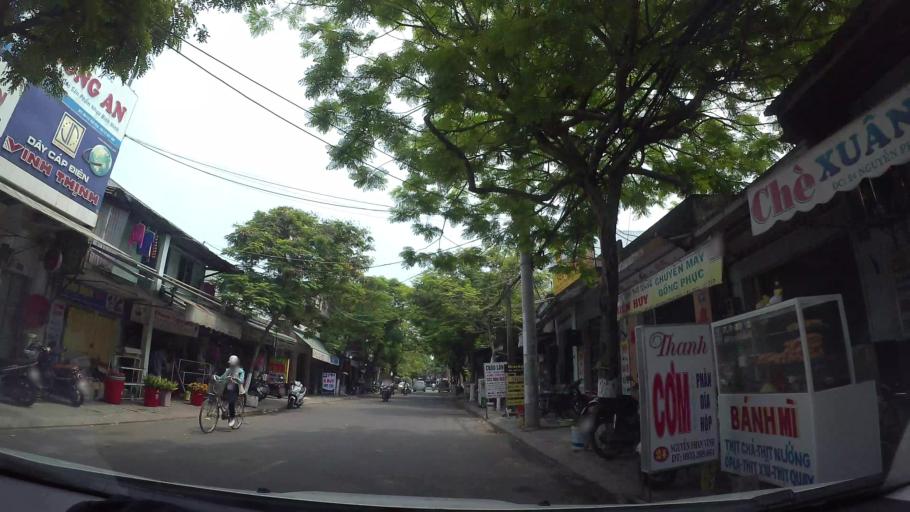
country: VN
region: Da Nang
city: Son Tra
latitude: 16.1009
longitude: 108.2501
